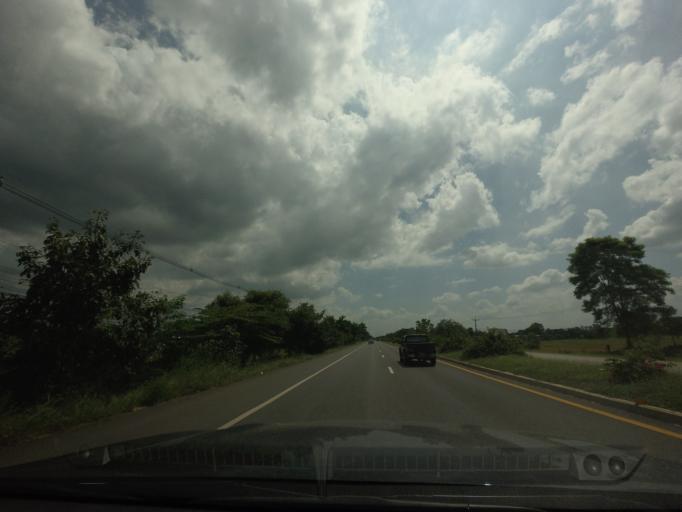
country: TH
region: Phetchabun
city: Nong Phai
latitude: 16.2026
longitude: 101.0890
